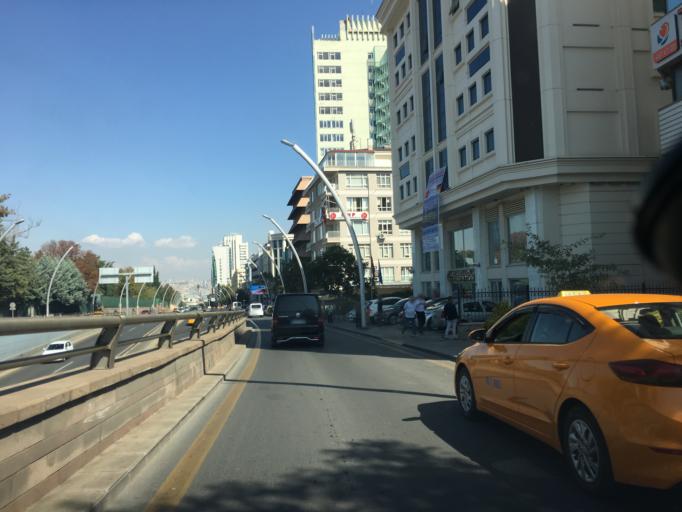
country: TR
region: Ankara
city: Cankaya
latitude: 39.9026
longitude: 32.8592
